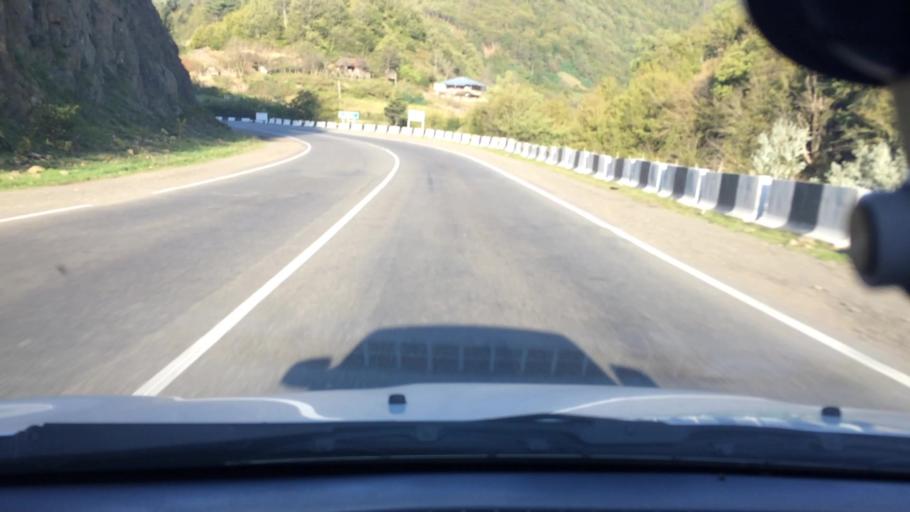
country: GE
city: Surami
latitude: 42.0994
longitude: 43.3935
